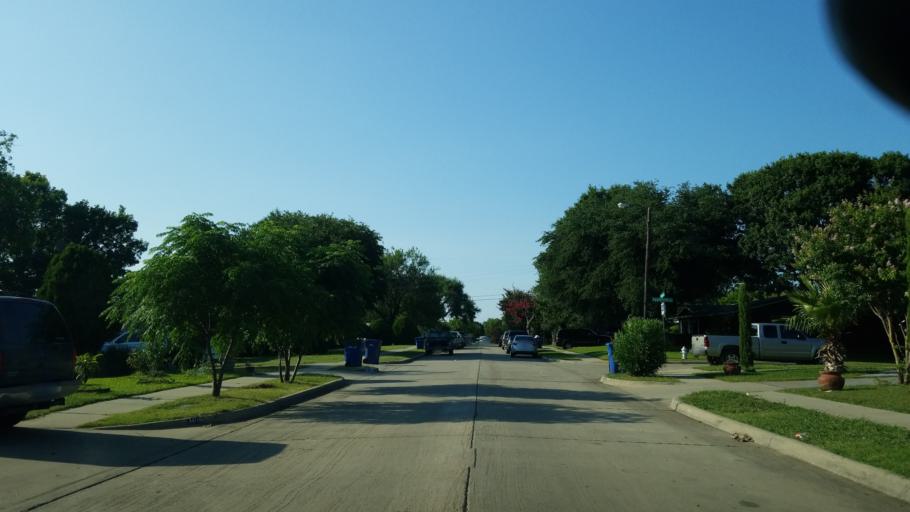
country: US
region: Texas
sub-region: Dallas County
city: Farmers Branch
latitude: 32.9411
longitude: -96.8985
